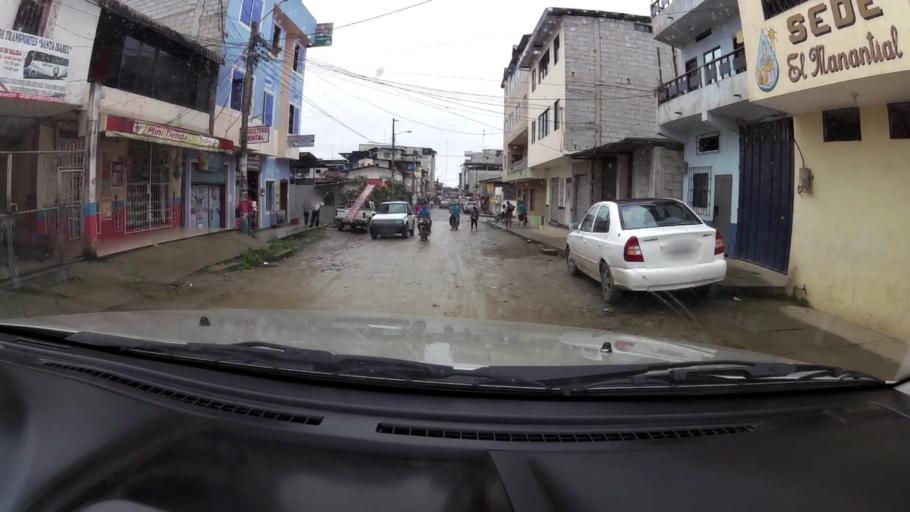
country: EC
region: Guayas
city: Balao
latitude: -3.0604
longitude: -79.7448
